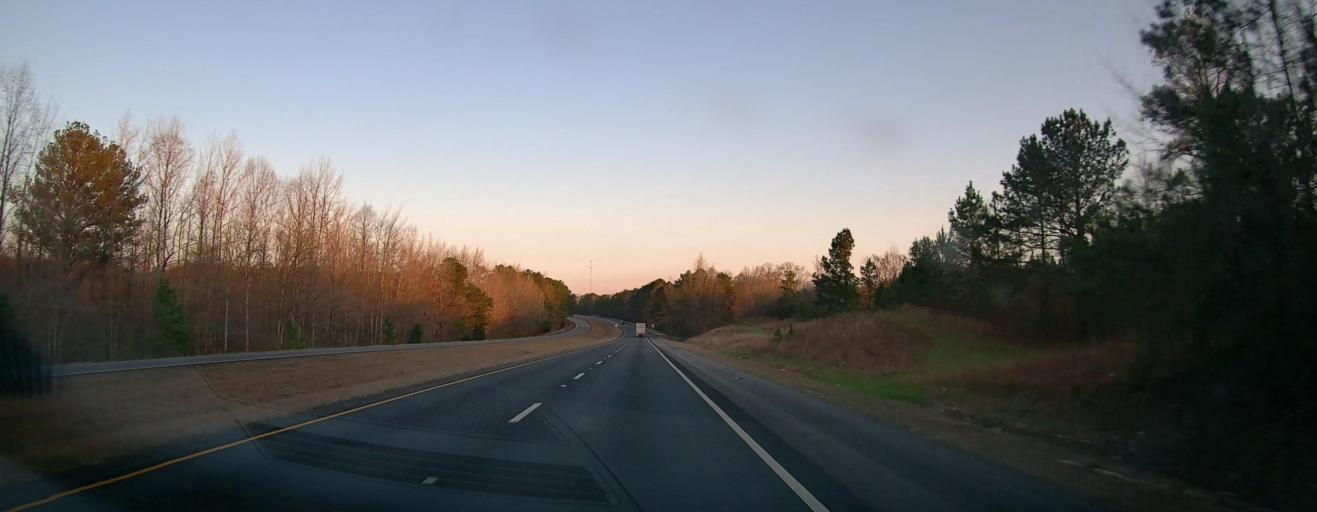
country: US
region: Alabama
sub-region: Coosa County
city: Goodwater
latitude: 33.0522
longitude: -86.1435
